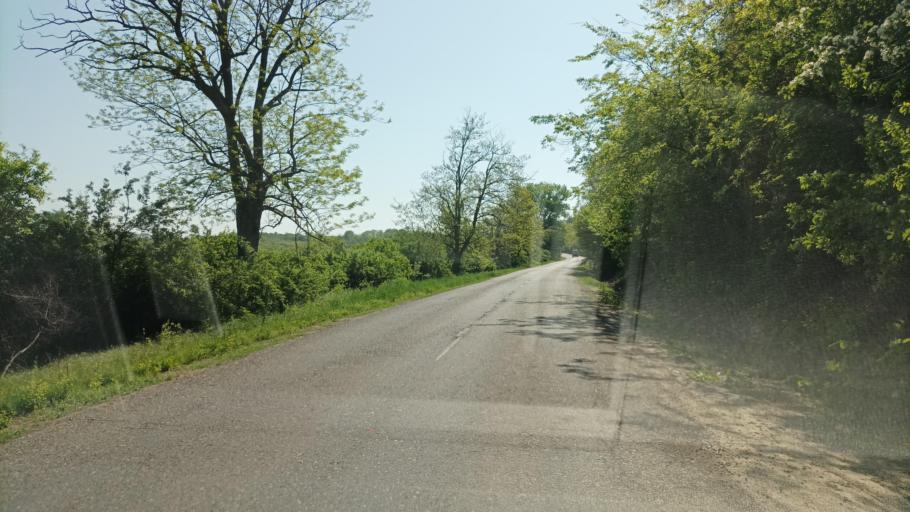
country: HU
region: Pest
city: Gomba
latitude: 47.3622
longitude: 19.5760
